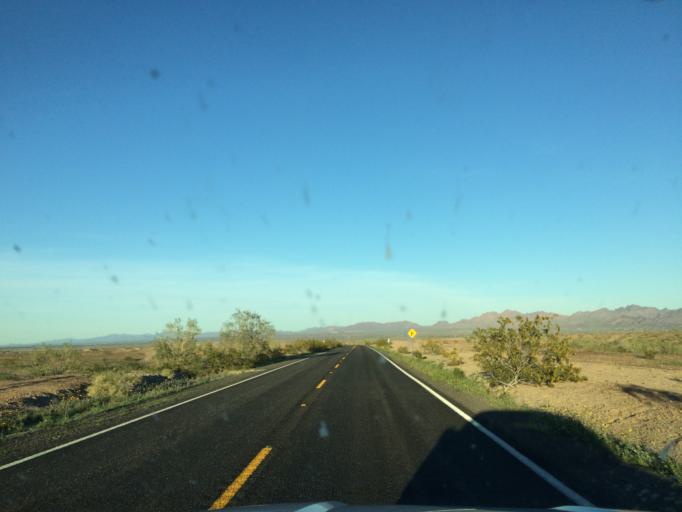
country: US
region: California
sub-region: Riverside County
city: Mesa Verde
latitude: 33.2887
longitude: -114.7605
